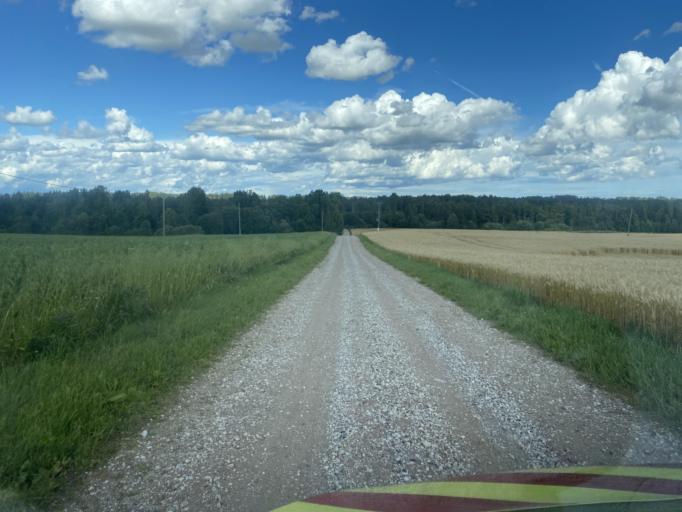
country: EE
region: Viljandimaa
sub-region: Viiratsi vald
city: Viiratsi
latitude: 58.2980
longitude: 25.6144
